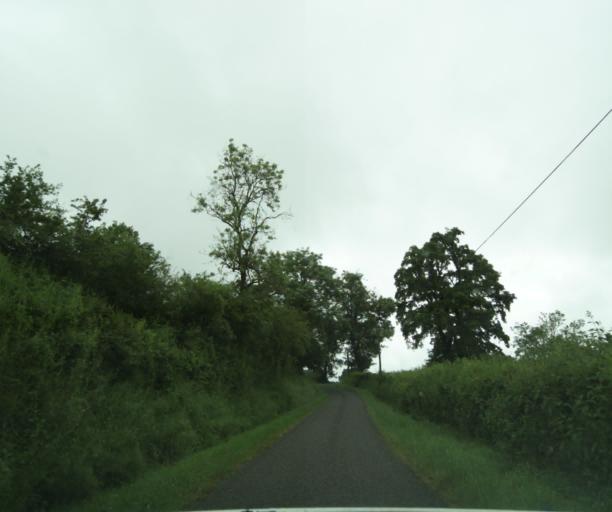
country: FR
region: Bourgogne
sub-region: Departement de Saone-et-Loire
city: Charolles
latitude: 46.4363
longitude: 4.3173
